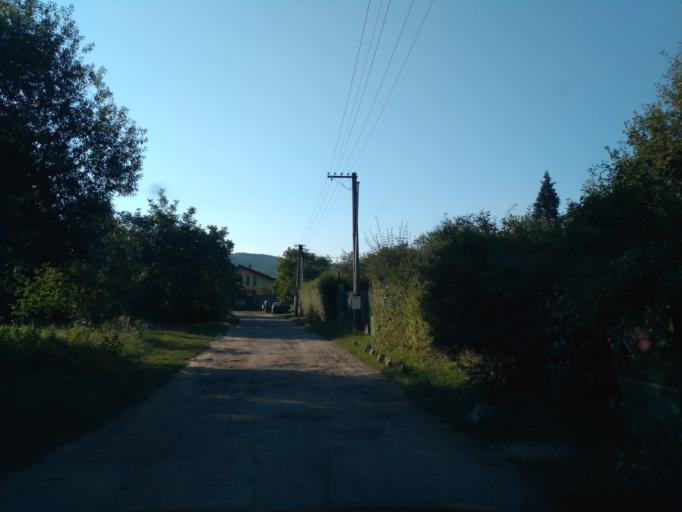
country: SK
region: Kosicky
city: Kosice
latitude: 48.7243
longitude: 21.2192
